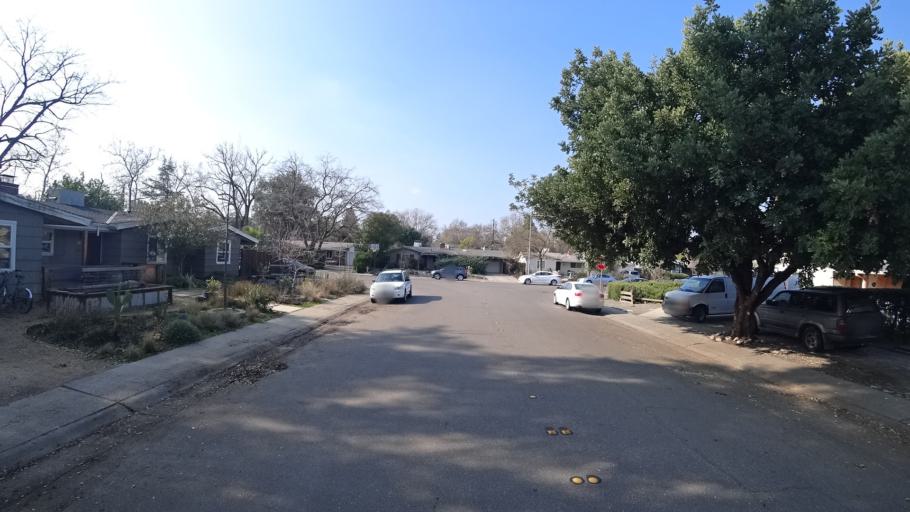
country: US
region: California
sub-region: Yolo County
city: Davis
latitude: 38.5478
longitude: -121.7572
